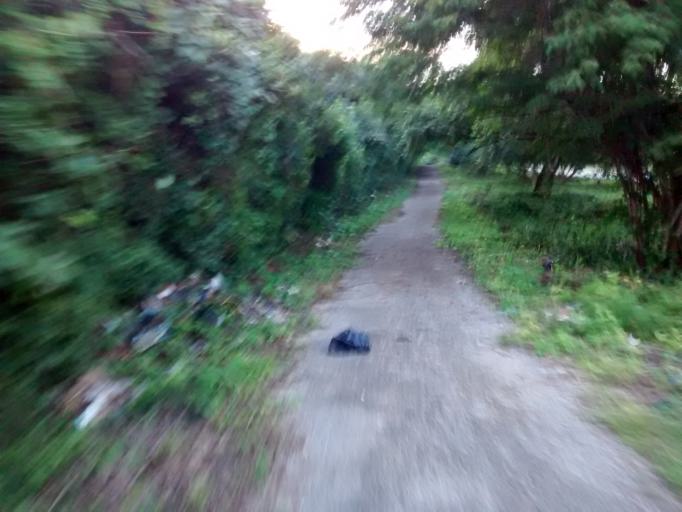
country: MX
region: Yucatan
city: Valladolid
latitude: 20.6925
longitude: -88.2234
